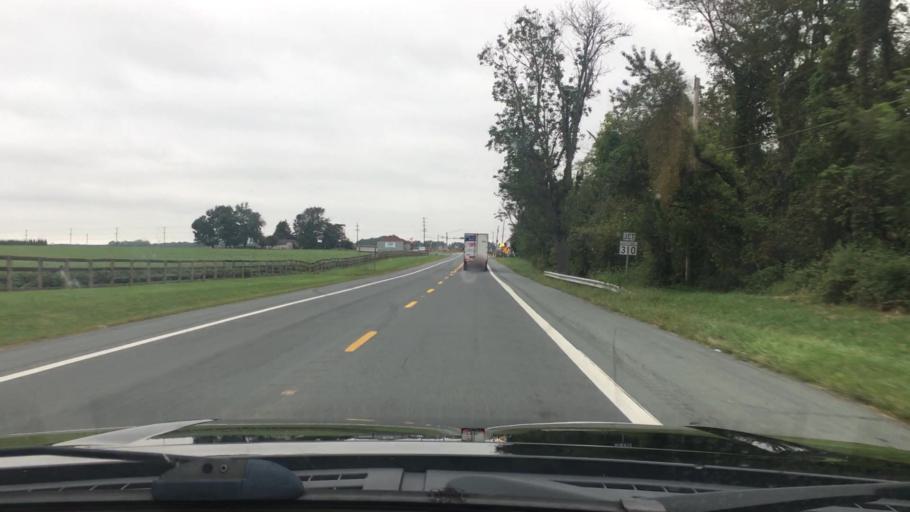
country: US
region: Maryland
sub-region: Cecil County
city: Elkton
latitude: 39.4829
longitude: -75.8482
